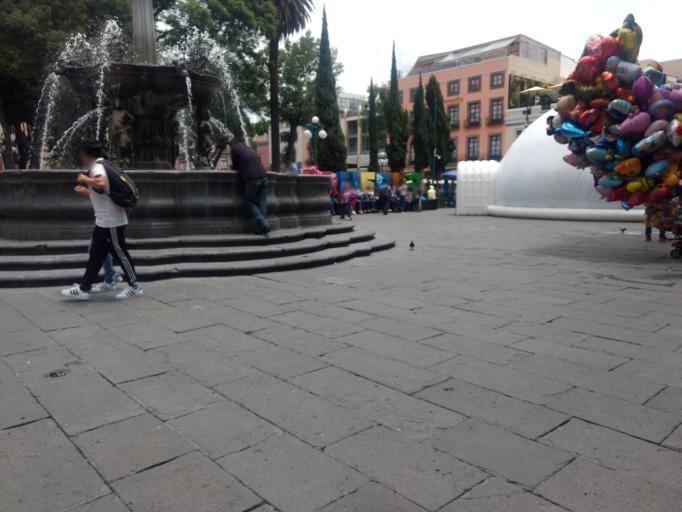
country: MX
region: Puebla
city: Puebla
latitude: 19.0436
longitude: -98.1980
